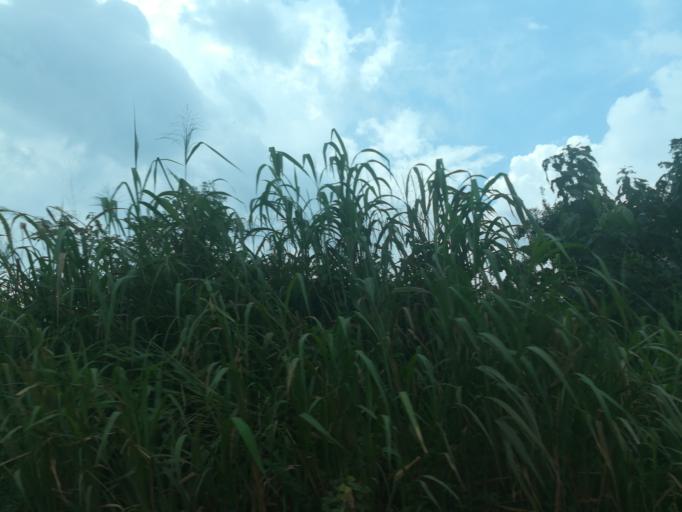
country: NG
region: Lagos
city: Ikorodu
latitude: 6.6706
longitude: 3.6447
